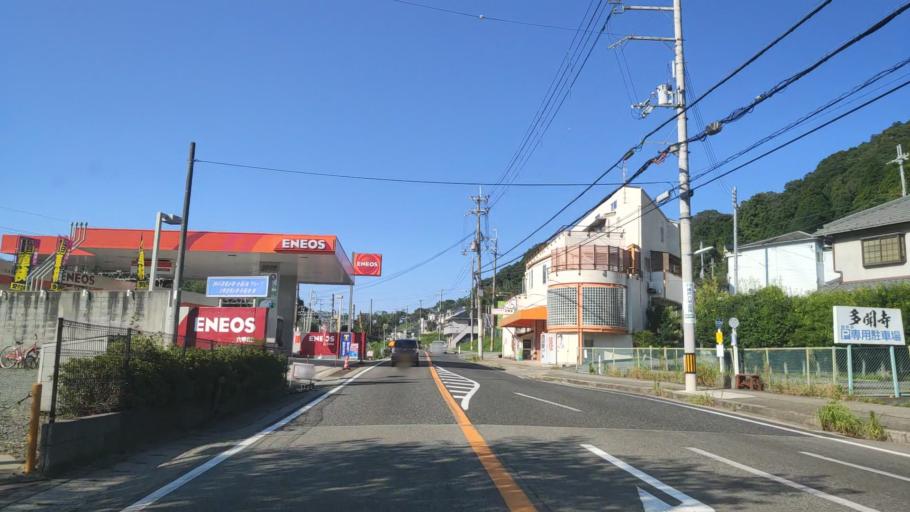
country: JP
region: Hyogo
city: Kobe
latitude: 34.7860
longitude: 135.2067
